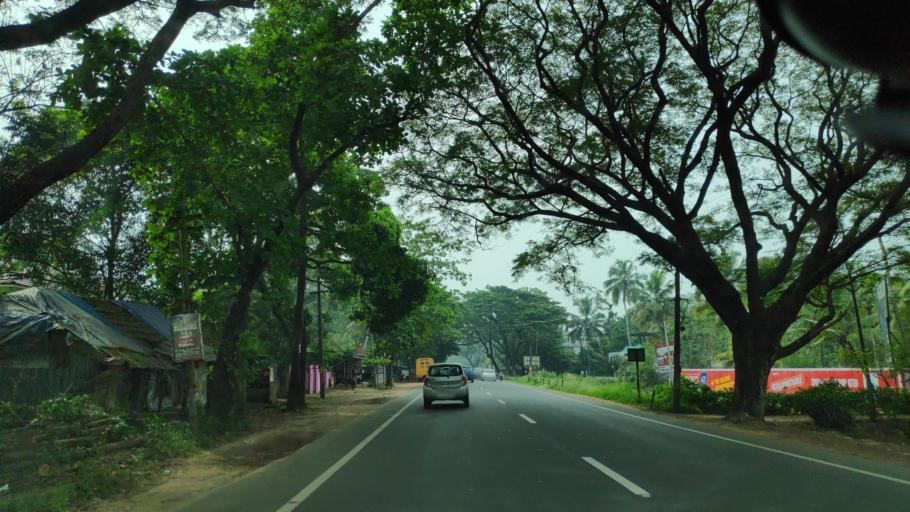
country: IN
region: Kerala
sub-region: Alappuzha
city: Alleppey
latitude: 9.5283
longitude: 76.3275
